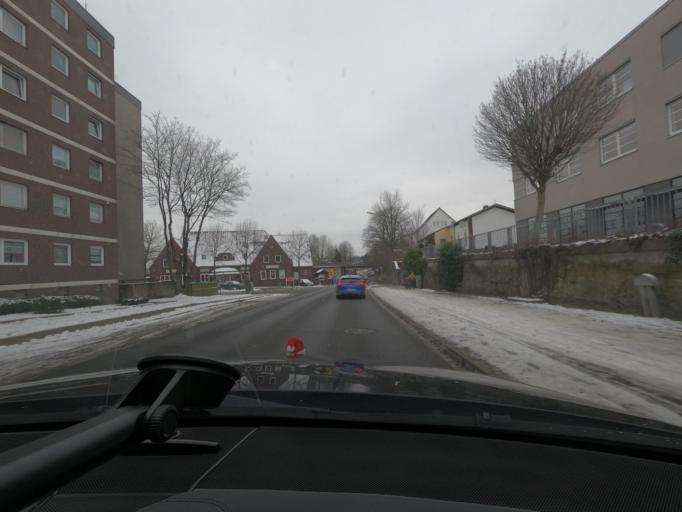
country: DE
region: Schleswig-Holstein
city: Jarplund-Weding
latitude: 54.7578
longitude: 9.3999
